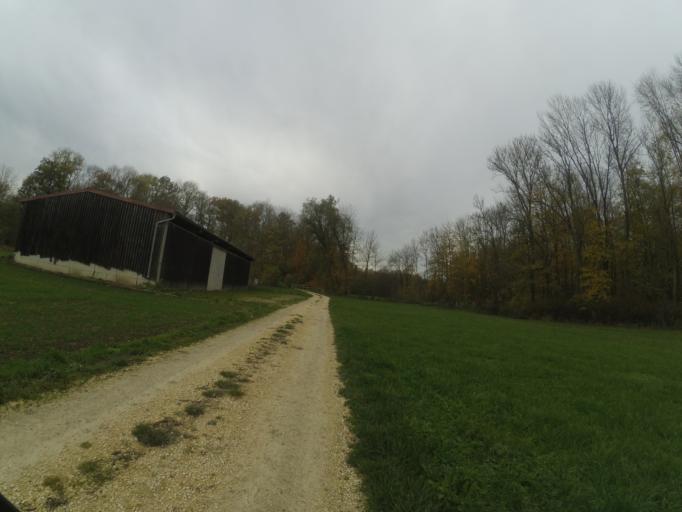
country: DE
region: Bavaria
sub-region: Swabia
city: Senden
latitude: 48.3434
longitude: 10.0038
